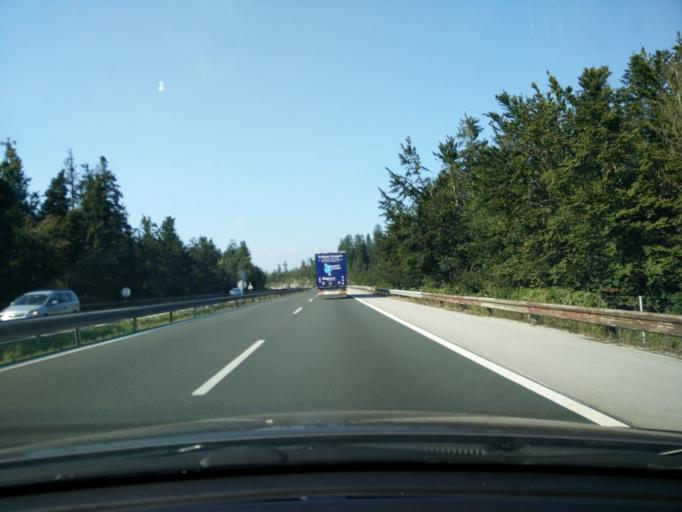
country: SI
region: Logatec
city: Logatec
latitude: 45.8785
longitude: 14.2629
